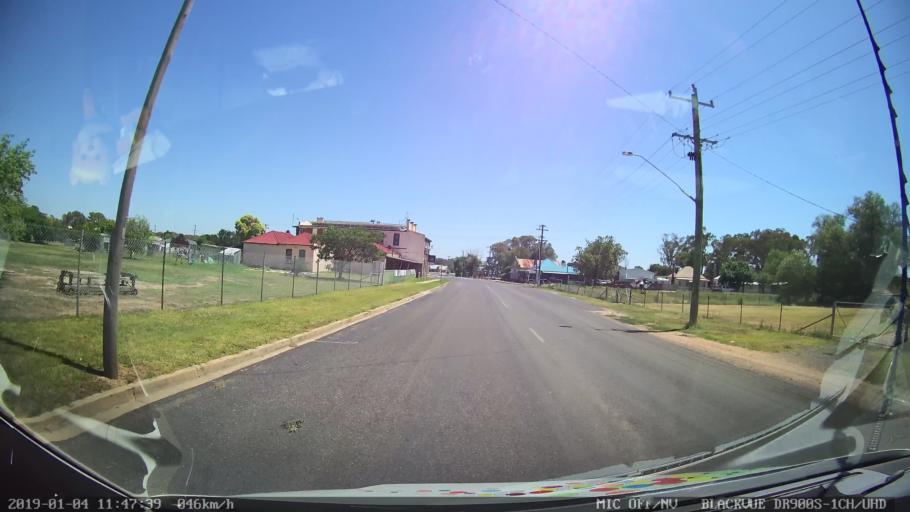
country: AU
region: New South Wales
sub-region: Cabonne
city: Molong
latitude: -32.9314
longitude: 148.7548
